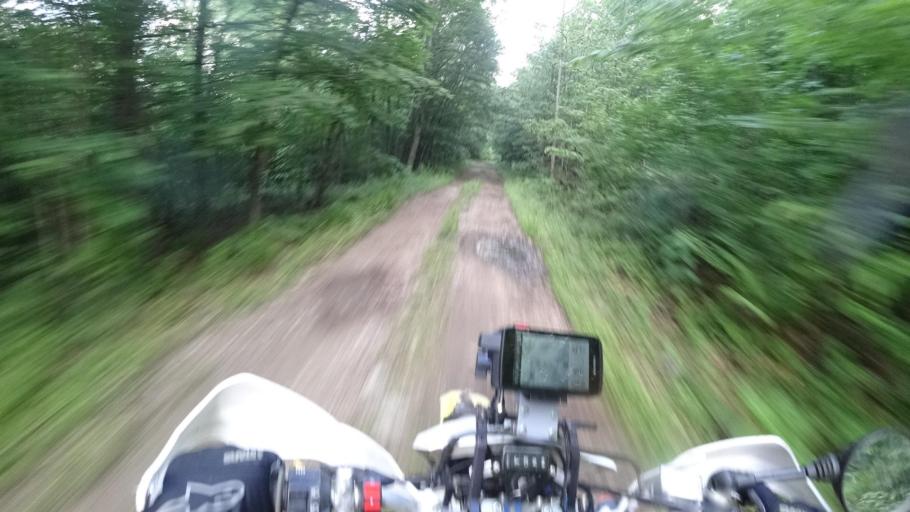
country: BA
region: Federation of Bosnia and Herzegovina
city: Bosanska Krupa
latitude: 44.7671
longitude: 16.3119
